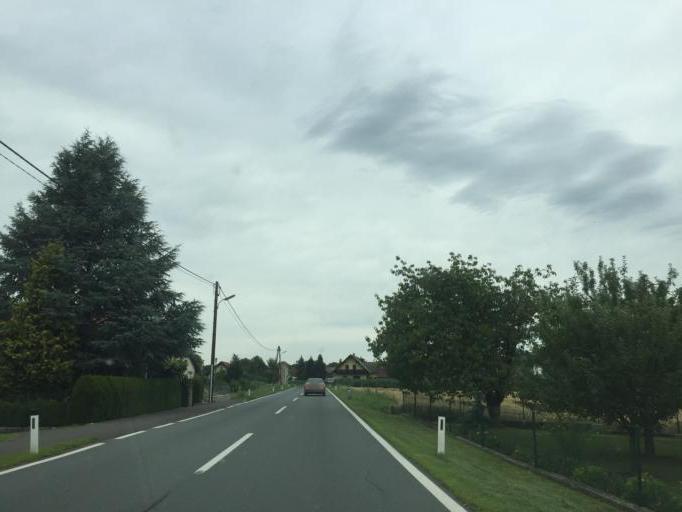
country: AT
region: Styria
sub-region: Politischer Bezirk Suedoststeiermark
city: Mureck
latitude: 46.7119
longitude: 15.7866
